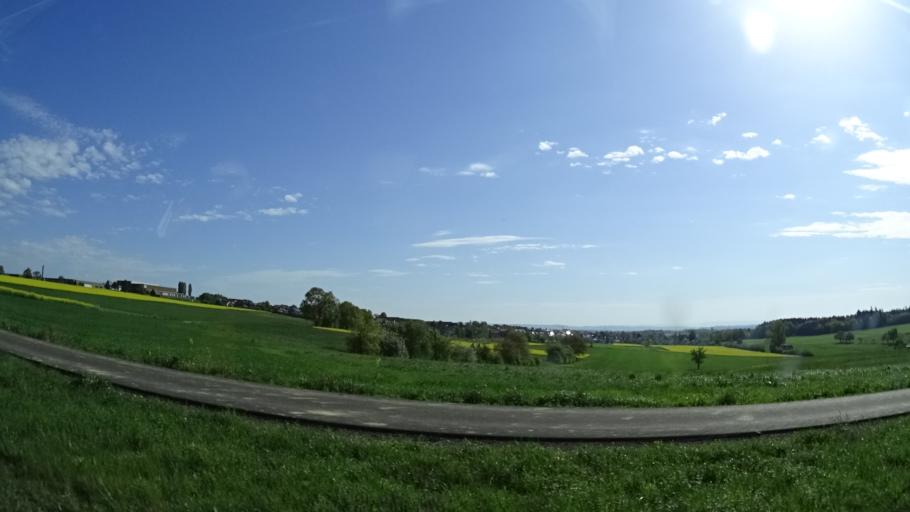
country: DE
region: Baden-Wuerttemberg
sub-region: Regierungsbezirk Stuttgart
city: Motzingen
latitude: 48.5280
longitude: 8.7615
